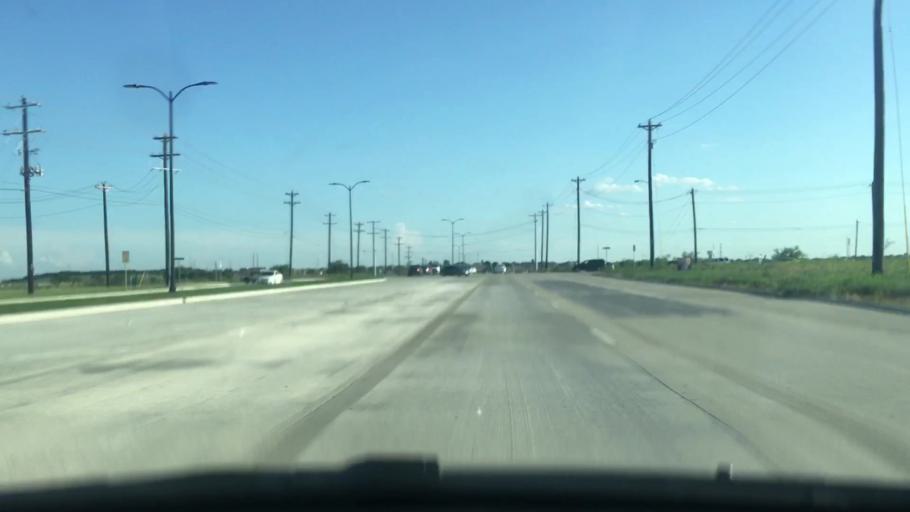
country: US
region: Texas
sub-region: Denton County
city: Little Elm
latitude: 33.2118
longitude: -96.8806
